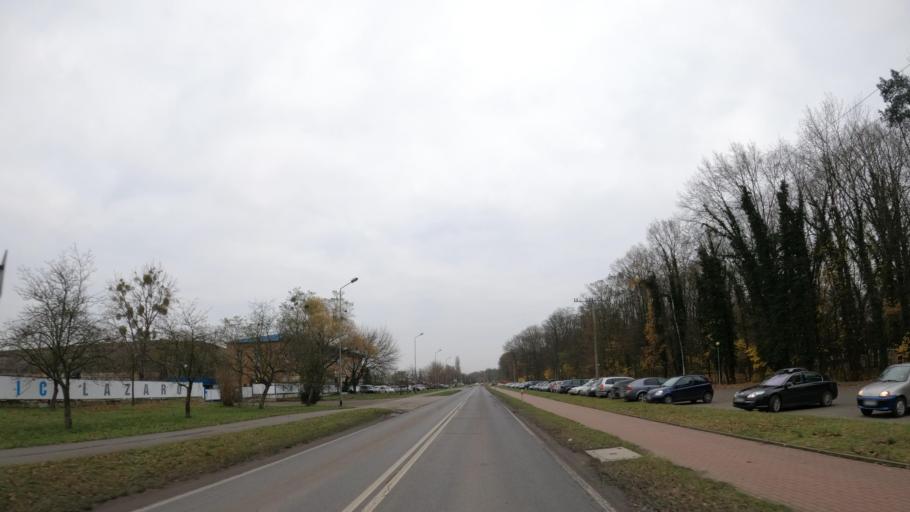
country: PL
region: West Pomeranian Voivodeship
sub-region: Powiat policki
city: Police
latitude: 53.5509
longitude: 14.5514
